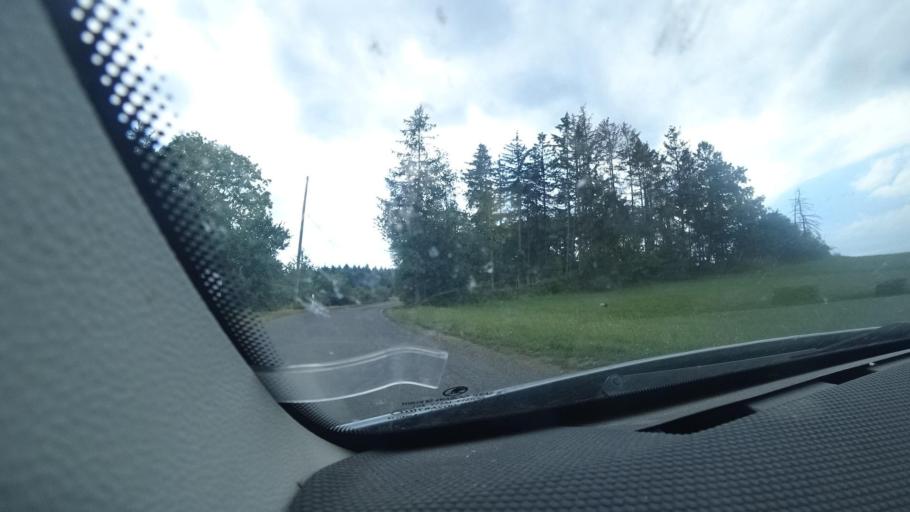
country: DE
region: Rheinland-Pfalz
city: Spessart
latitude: 50.4673
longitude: 7.0897
